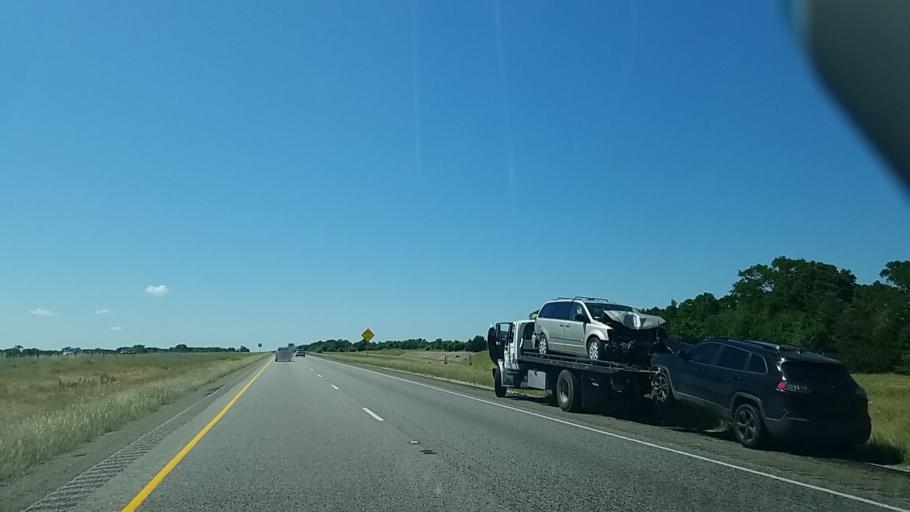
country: US
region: Texas
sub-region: Freestone County
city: Fairfield
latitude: 31.7694
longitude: -96.2191
